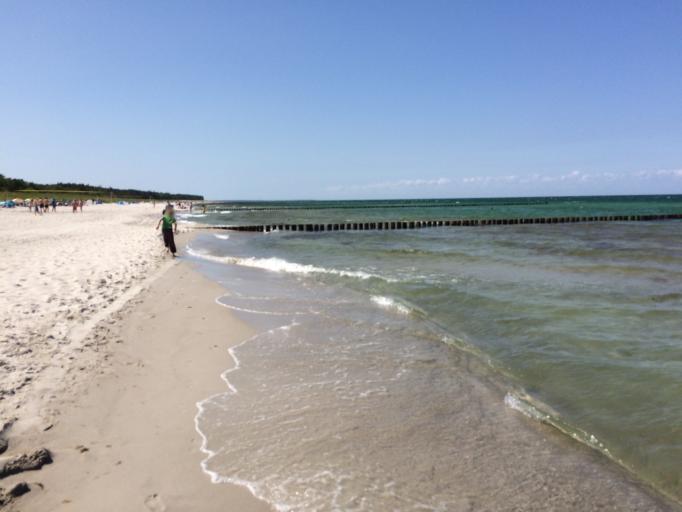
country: DE
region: Mecklenburg-Vorpommern
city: Zingst
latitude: 54.4436
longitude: 12.6533
